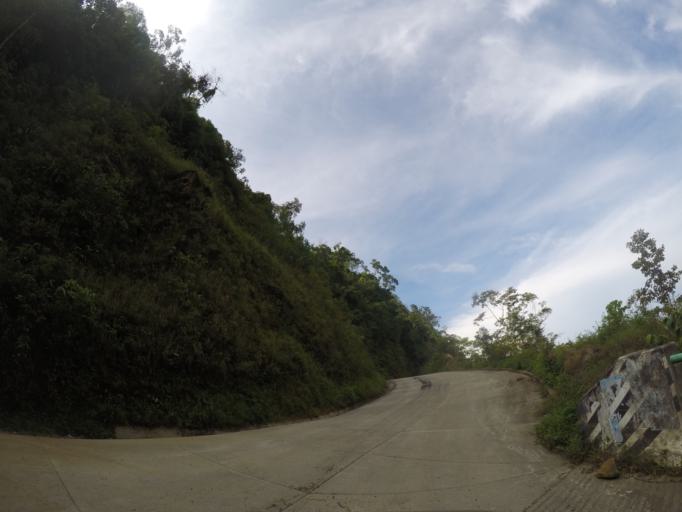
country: MX
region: Oaxaca
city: Pluma Hidalgo
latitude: 15.9396
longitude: -96.4303
